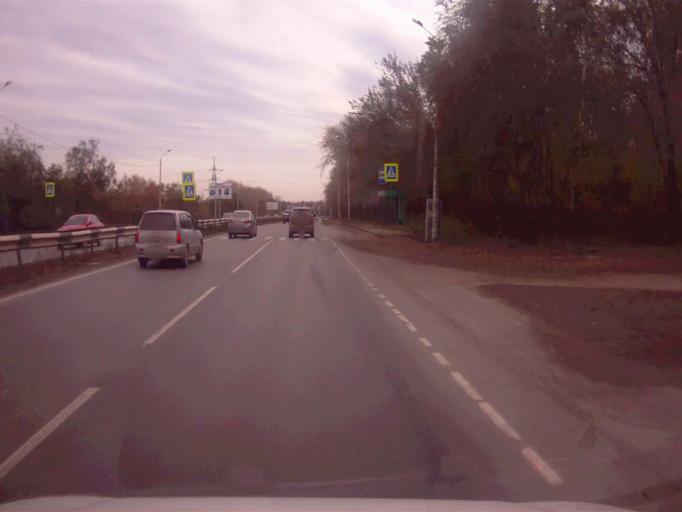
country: RU
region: Chelyabinsk
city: Novosineglazovskiy
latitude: 55.0521
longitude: 61.4111
